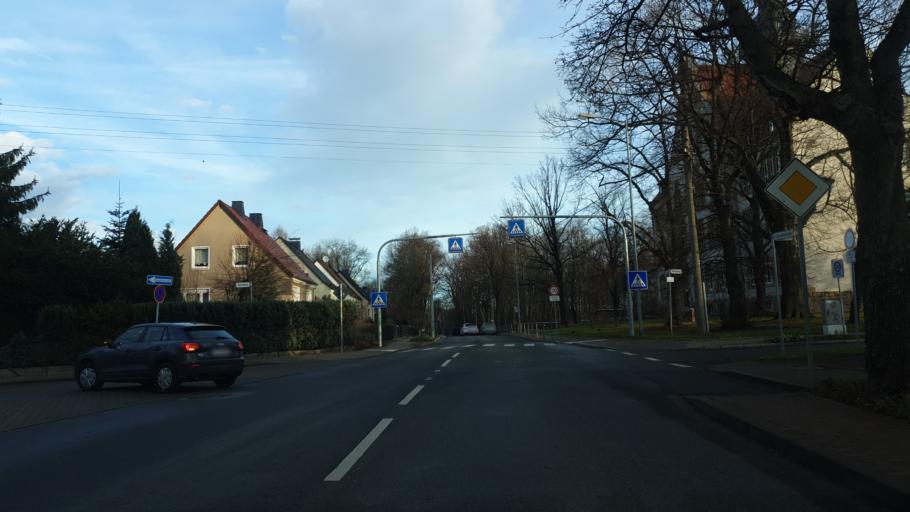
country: DE
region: Saxony
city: Neukirchen
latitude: 50.8267
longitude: 12.8337
